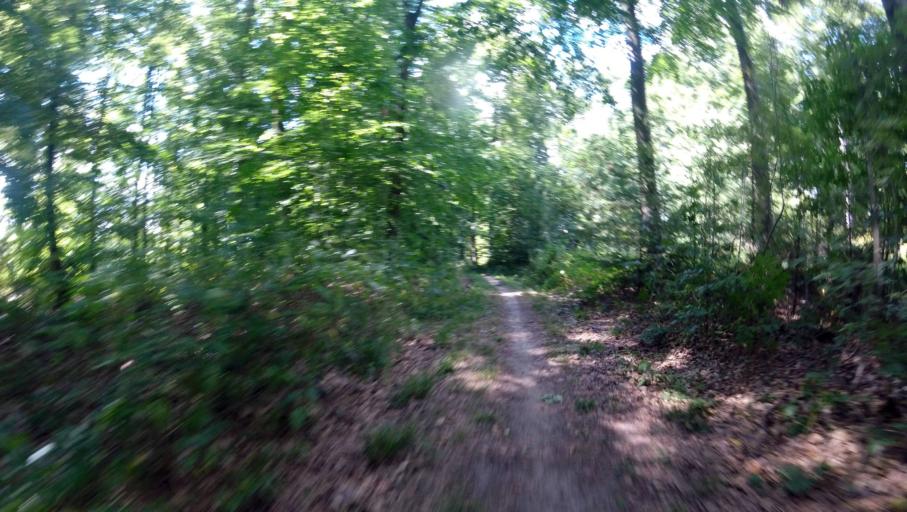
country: DE
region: Baden-Wuerttemberg
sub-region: Regierungsbezirk Stuttgart
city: Oppenweiler
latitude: 49.0091
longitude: 9.4463
